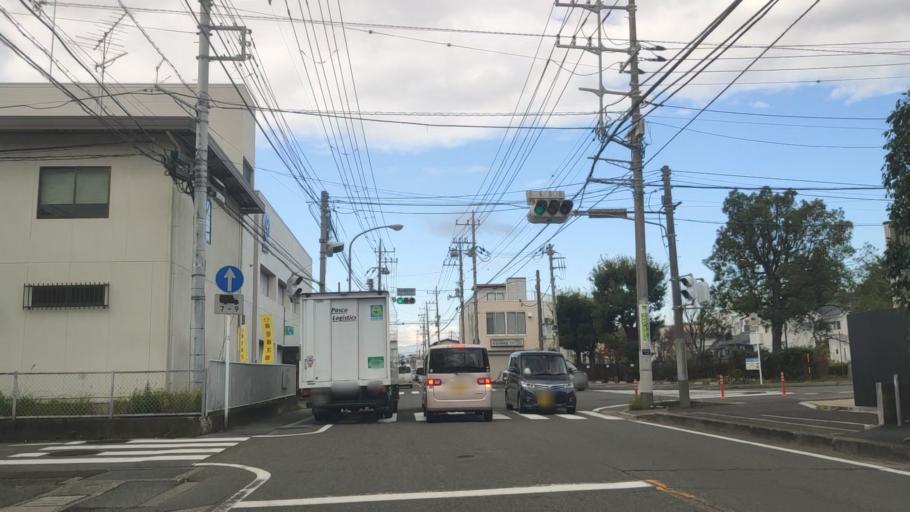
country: JP
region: Kanagawa
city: Minami-rinkan
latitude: 35.4266
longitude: 139.5268
